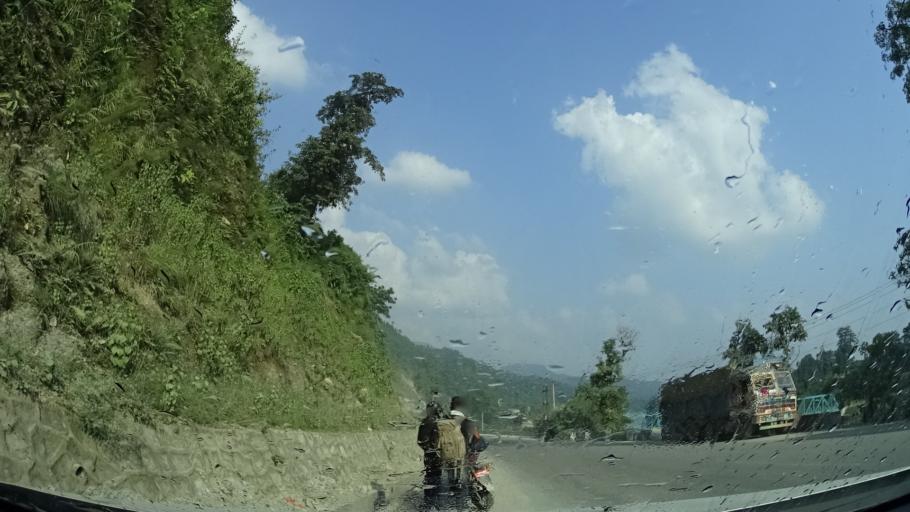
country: NP
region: Central Region
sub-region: Narayani Zone
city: Bharatpur
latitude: 27.7794
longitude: 84.4460
